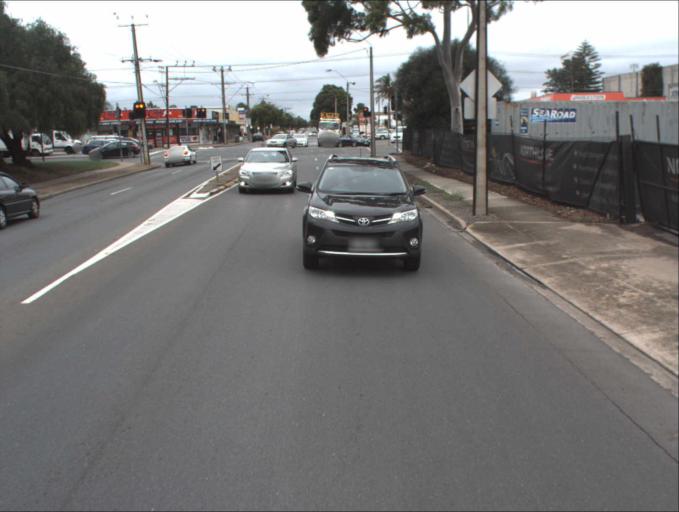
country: AU
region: South Australia
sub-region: Charles Sturt
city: Woodville
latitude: -34.8746
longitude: 138.5662
